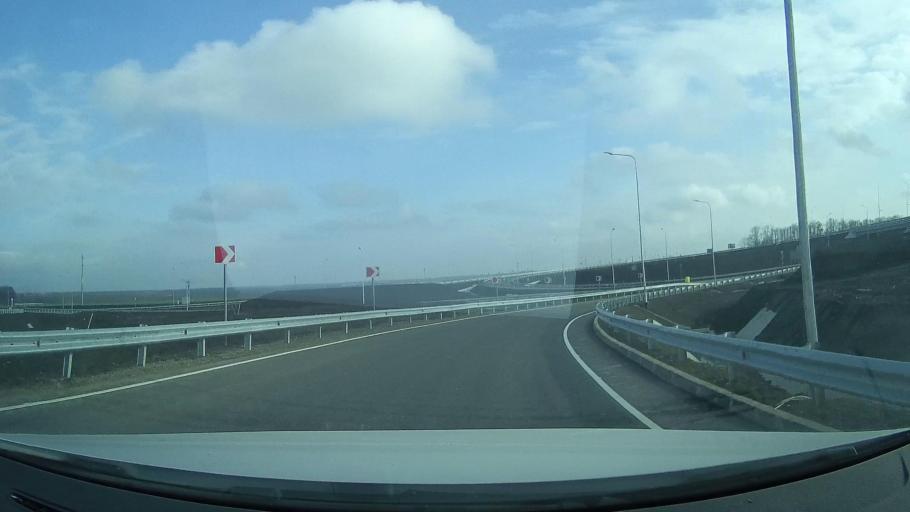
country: RU
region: Rostov
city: Grushevskaya
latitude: 47.3796
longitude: 39.8445
